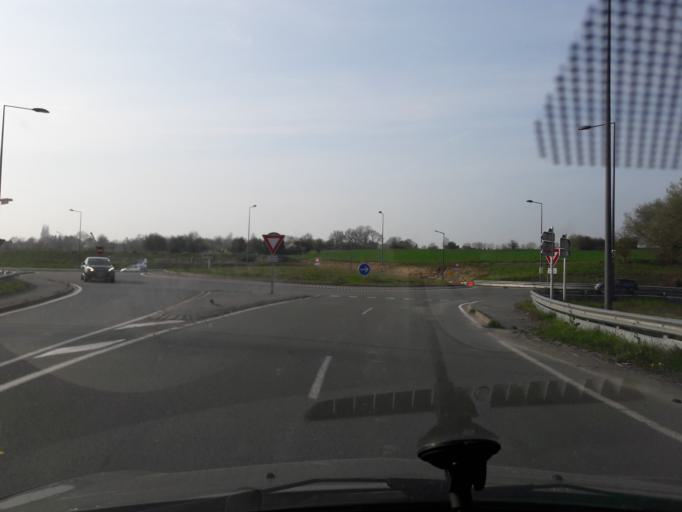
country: FR
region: Nord-Pas-de-Calais
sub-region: Departement du Nord
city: Rousies
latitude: 50.2795
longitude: 3.9960
